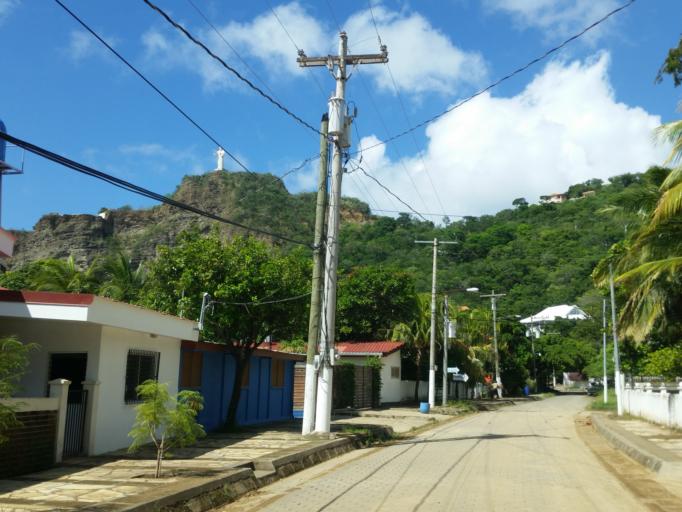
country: NI
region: Rivas
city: San Juan del Sur
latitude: 11.2616
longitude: -85.8776
